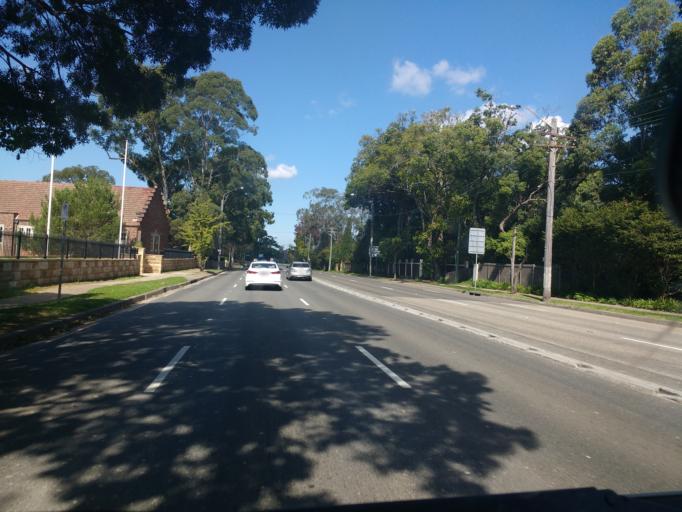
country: AU
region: New South Wales
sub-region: Ku-ring-gai
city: North Wahroonga
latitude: -33.7231
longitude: 151.1186
